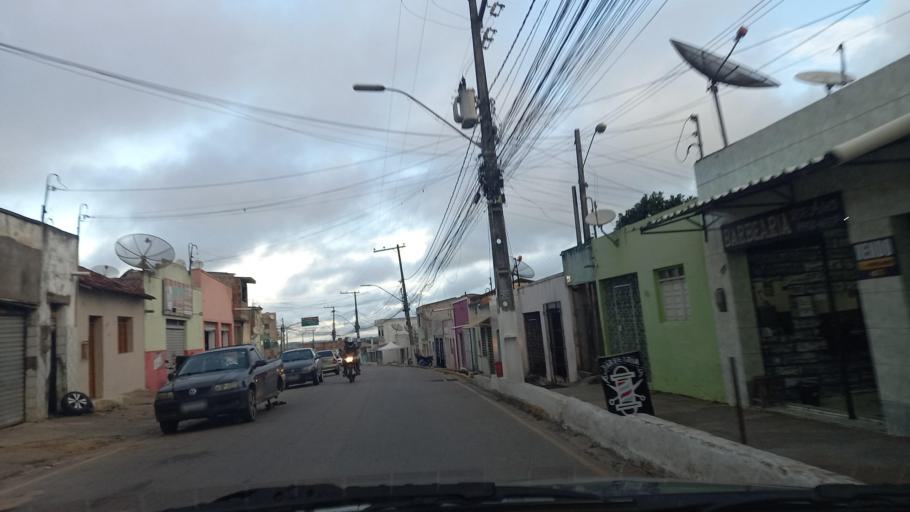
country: BR
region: Pernambuco
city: Garanhuns
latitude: -8.8818
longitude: -36.5059
